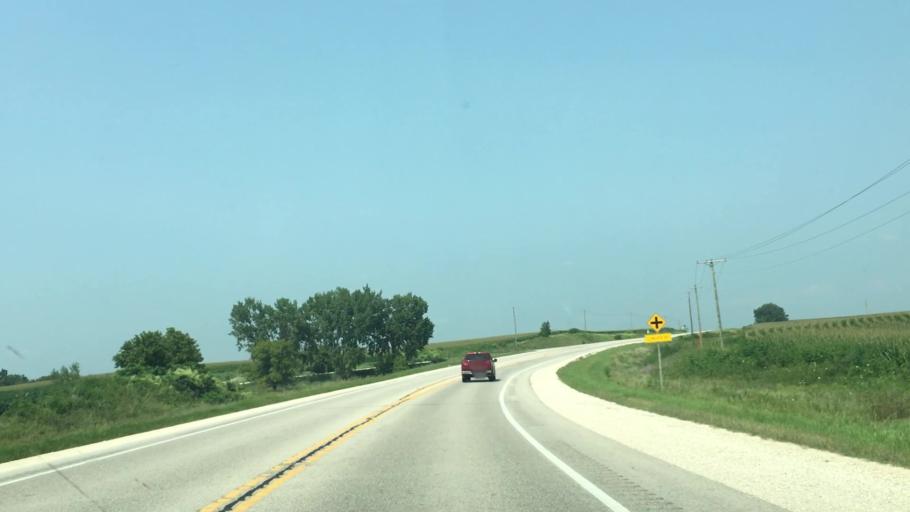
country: US
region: Iowa
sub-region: Winneshiek County
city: Decorah
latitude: 43.2103
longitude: -91.8788
